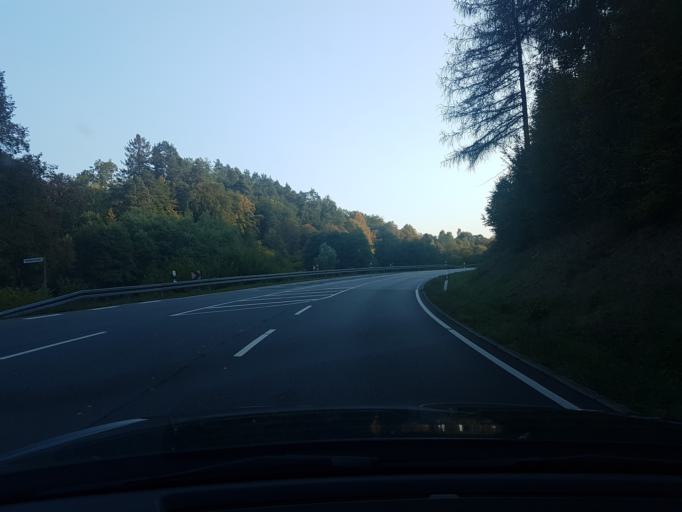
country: DE
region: Hesse
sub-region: Regierungsbezirk Darmstadt
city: Beerfelden
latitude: 49.6037
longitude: 8.9911
